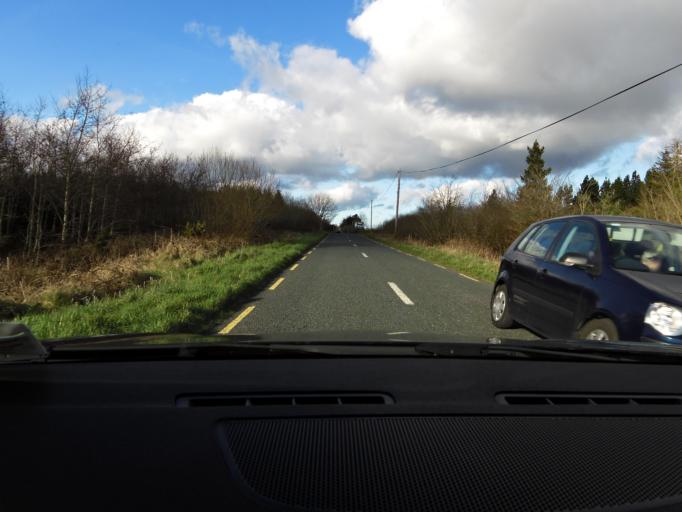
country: IE
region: Connaught
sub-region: Roscommon
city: Castlerea
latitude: 53.6636
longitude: -8.5051
